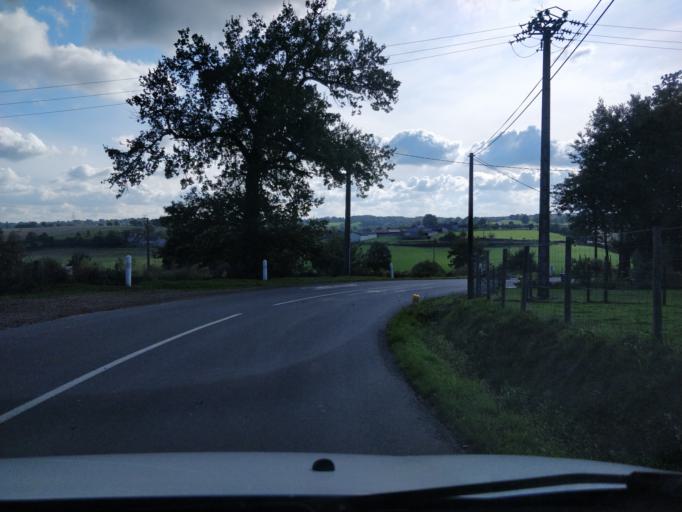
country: FR
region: Brittany
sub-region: Departement d'Ille-et-Vilaine
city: La Bouexiere
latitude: 48.1979
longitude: -1.4216
